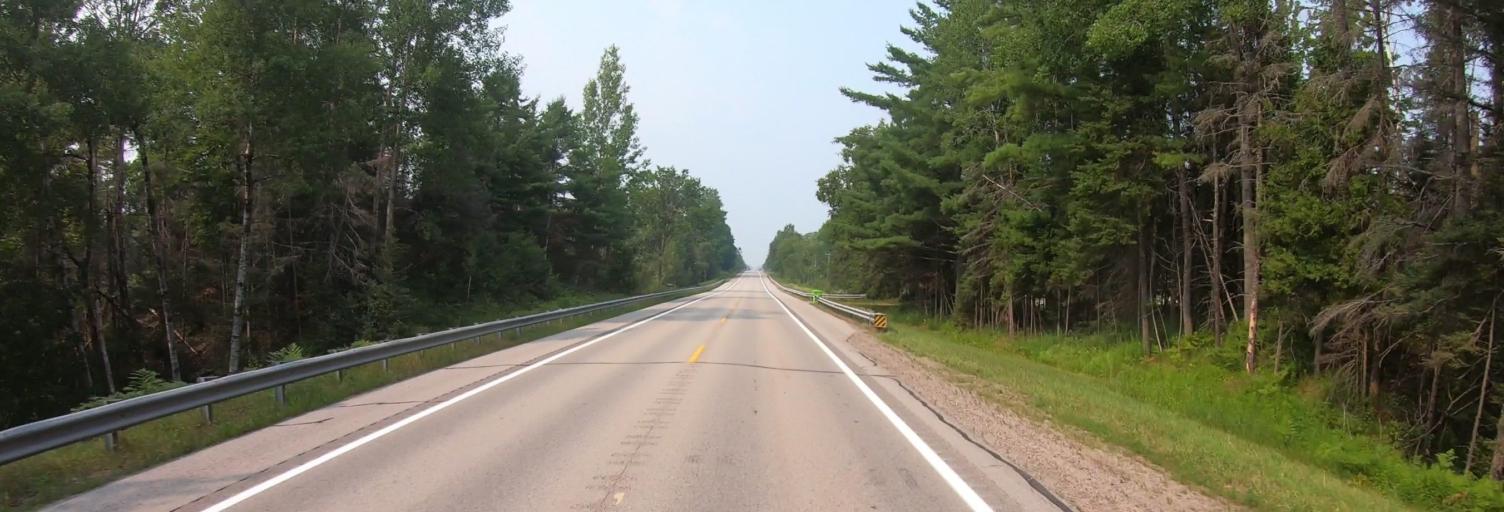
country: US
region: Michigan
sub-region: Chippewa County
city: Sault Ste. Marie
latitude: 46.2479
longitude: -84.3634
